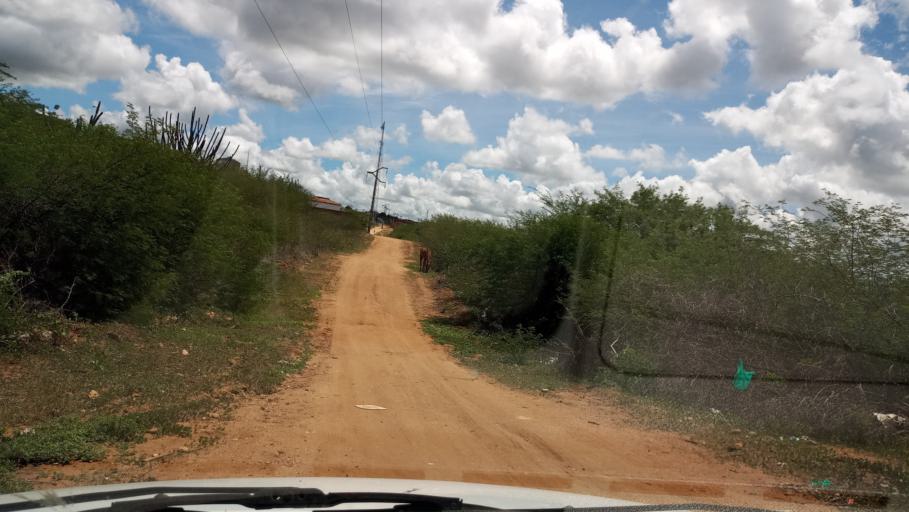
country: BR
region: Rio Grande do Norte
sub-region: Sao Paulo Do Potengi
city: Sao Paulo do Potengi
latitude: -5.9039
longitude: -35.7719
